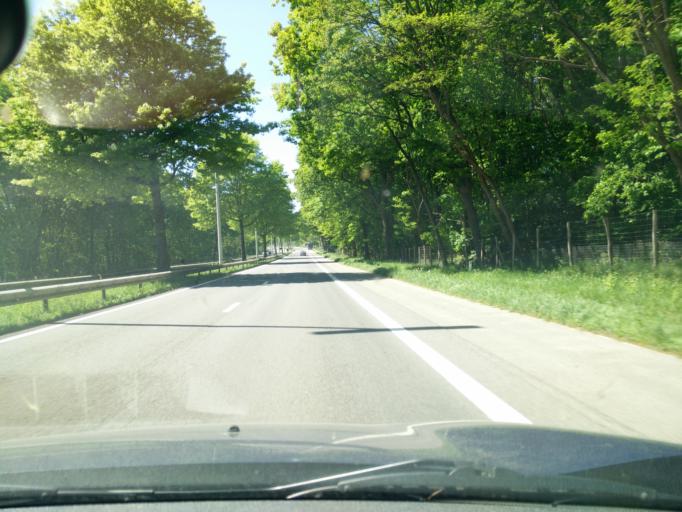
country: BE
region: Flanders
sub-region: Provincie Limburg
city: Maasmechelen
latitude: 51.0153
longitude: 5.6815
